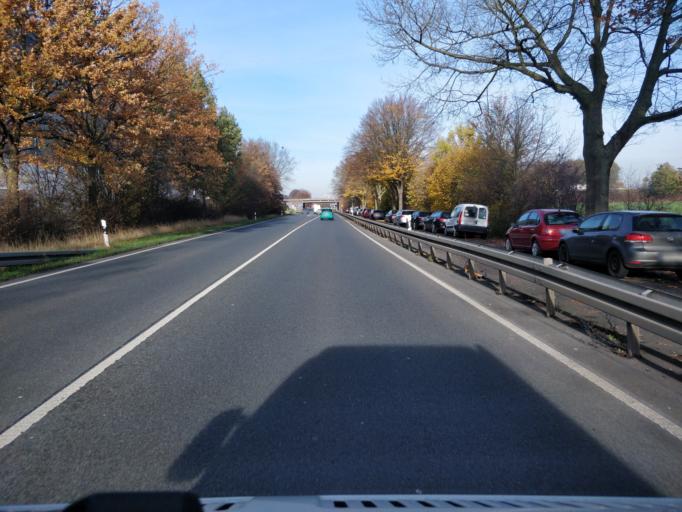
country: DE
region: North Rhine-Westphalia
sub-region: Regierungsbezirk Dusseldorf
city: Hamminkeln
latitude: 51.7454
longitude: 6.5909
